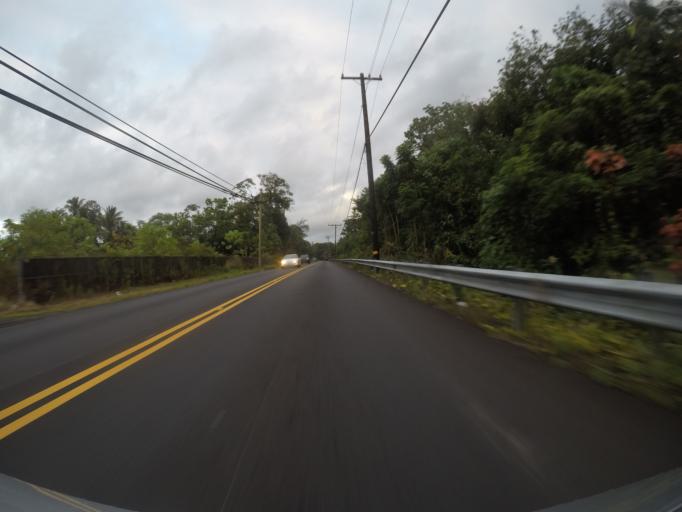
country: US
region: Hawaii
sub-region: Hawaii County
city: Kea'au
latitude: 19.6725
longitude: -155.0659
